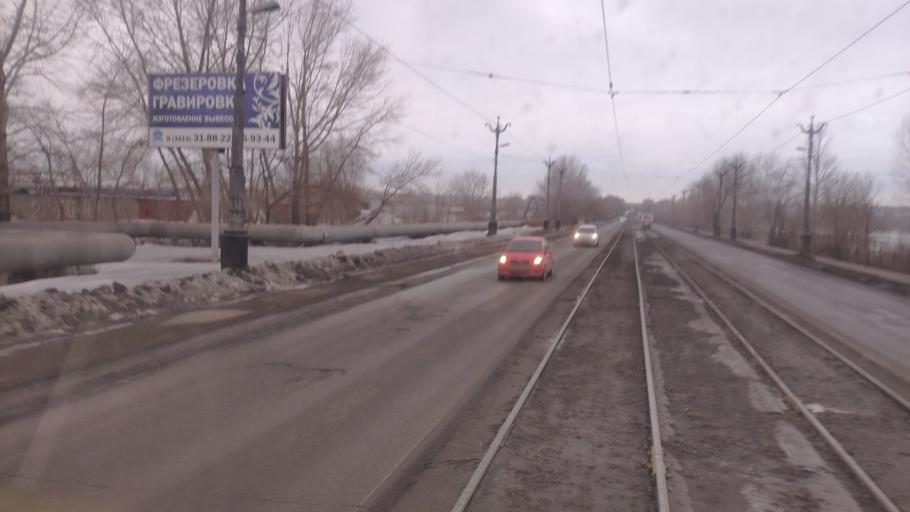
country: RU
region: Chelyabinsk
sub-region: Gorod Magnitogorsk
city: Magnitogorsk
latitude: 53.4222
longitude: 59.0205
